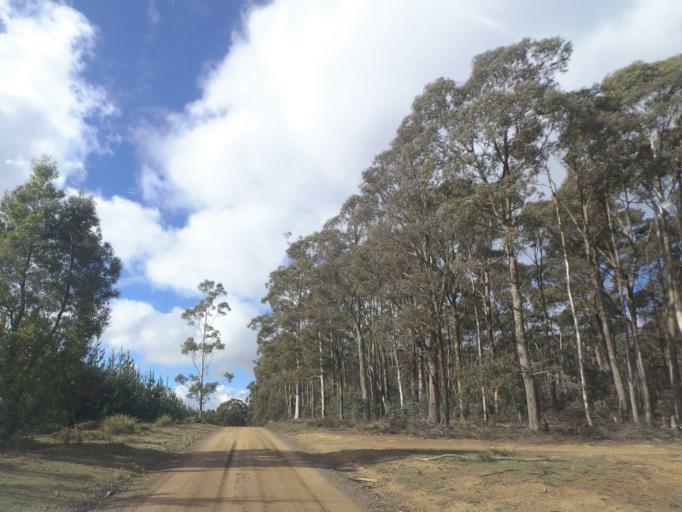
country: AU
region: Victoria
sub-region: Moorabool
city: Bacchus Marsh
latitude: -37.4310
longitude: 144.4428
